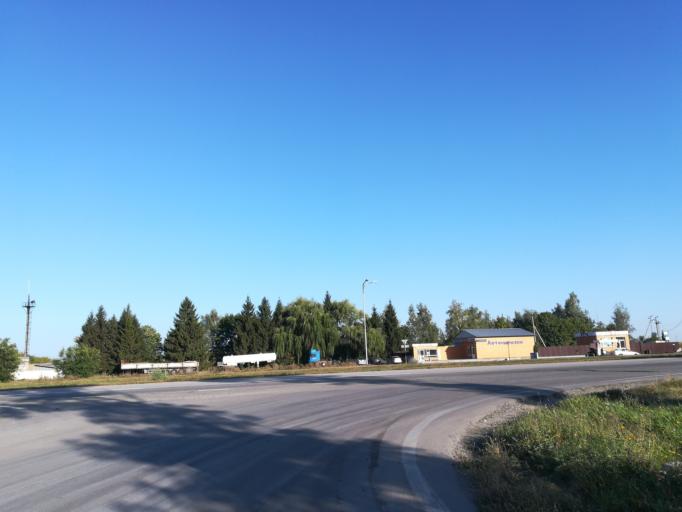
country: RU
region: Belgorod
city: Bekhteyevka
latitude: 50.7941
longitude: 37.1428
